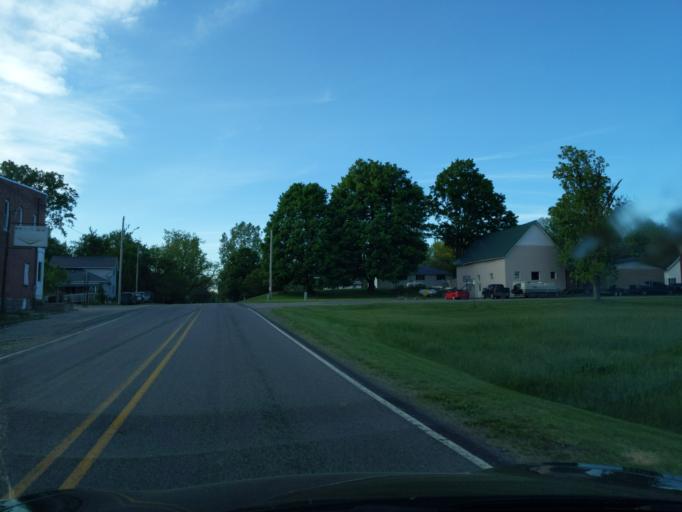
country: US
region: Michigan
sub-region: Ingham County
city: Leslie
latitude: 42.4748
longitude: -84.3170
